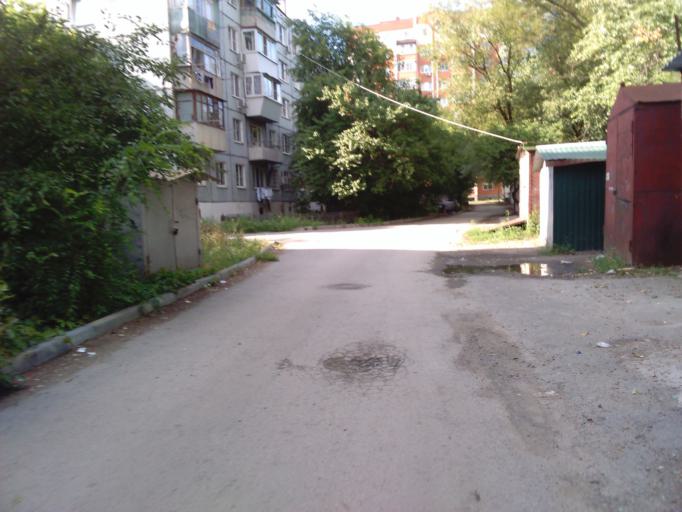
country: RU
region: Rostov
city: Bataysk
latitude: 47.1274
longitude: 39.7369
